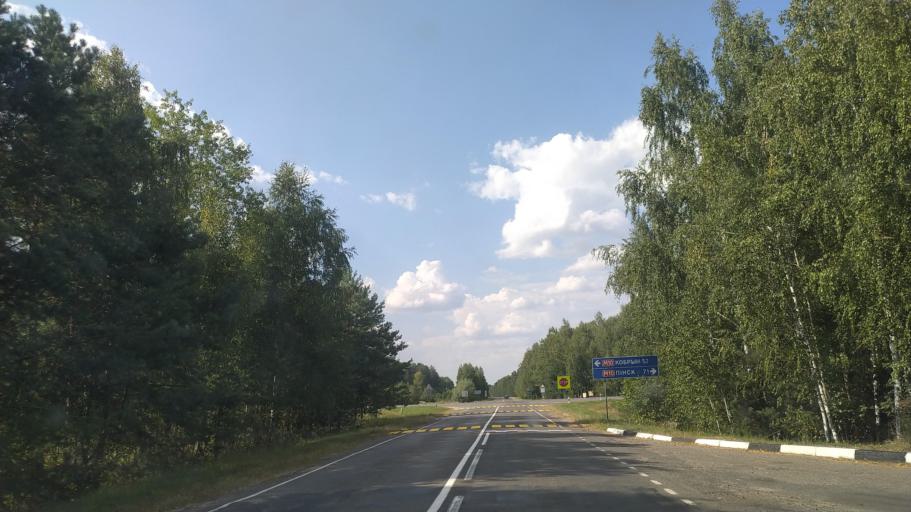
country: BY
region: Brest
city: Drahichyn
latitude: 52.2211
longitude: 25.1249
